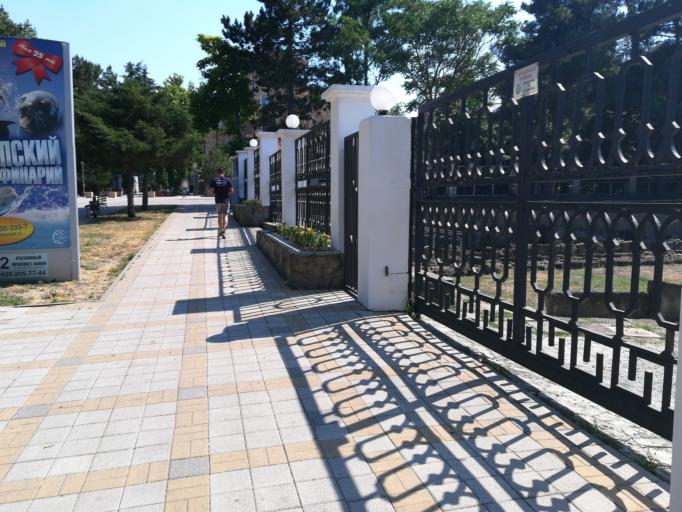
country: RU
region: Krasnodarskiy
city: Anapa
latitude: 44.8960
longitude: 37.3113
